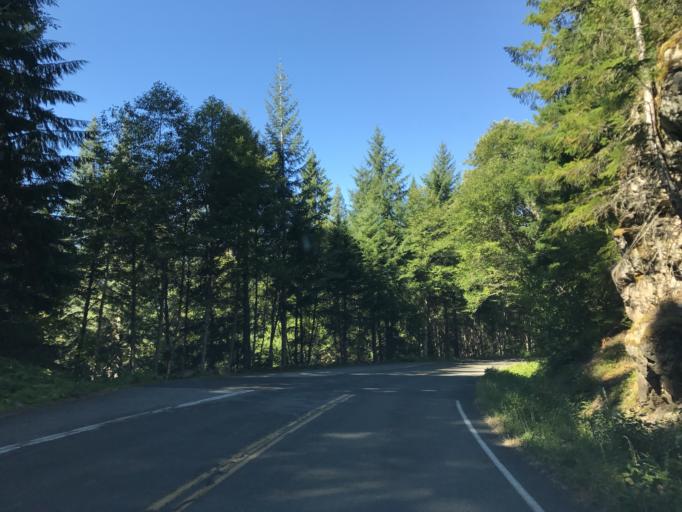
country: US
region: Washington
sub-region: Pierce County
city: Buckley
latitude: 46.7349
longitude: -121.6148
